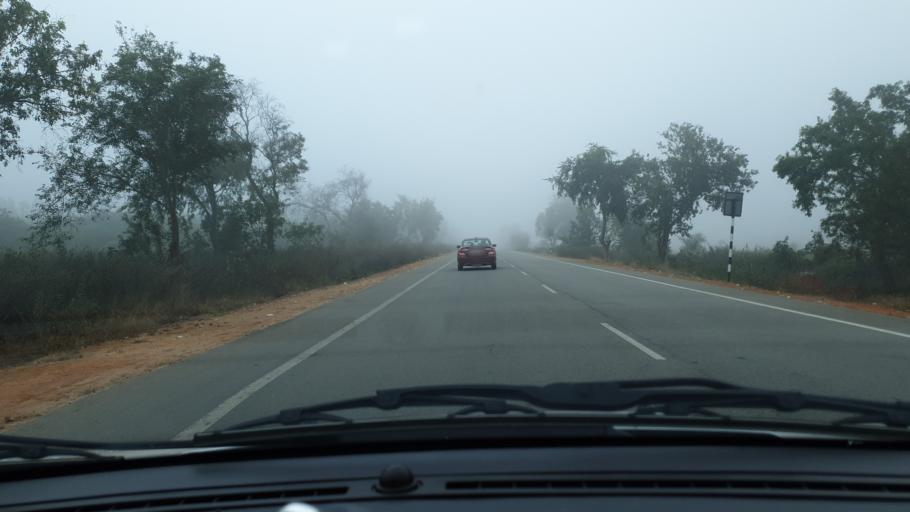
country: IN
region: Telangana
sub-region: Mahbubnagar
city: Nagar Karnul
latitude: 16.6587
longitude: 78.5766
